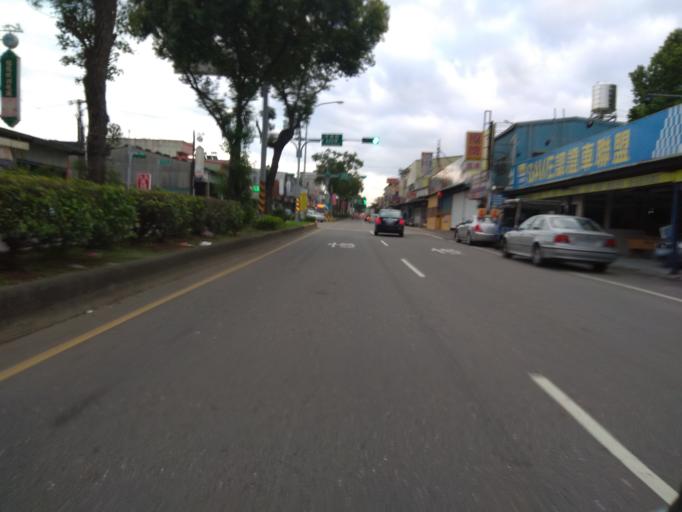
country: TW
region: Taiwan
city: Daxi
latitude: 24.8875
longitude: 121.2124
